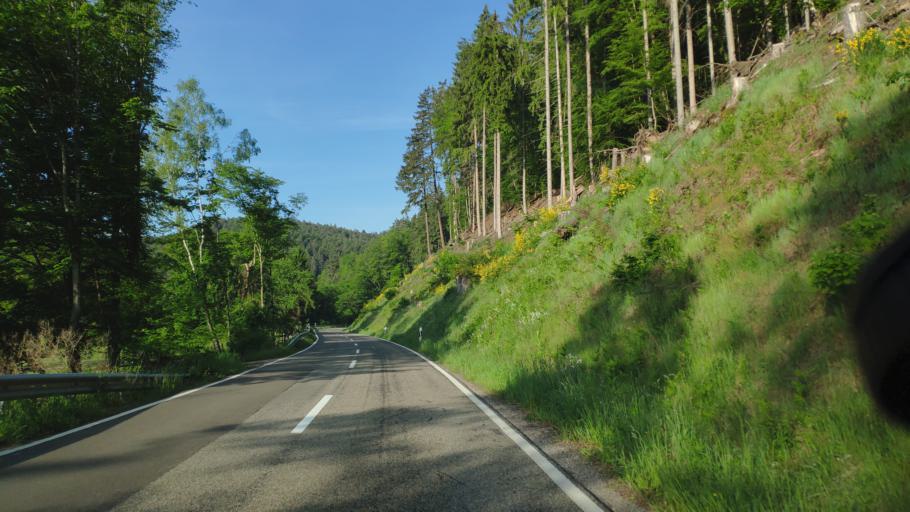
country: DE
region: Rheinland-Pfalz
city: Hinterweidenthal
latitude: 49.1832
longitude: 7.7215
